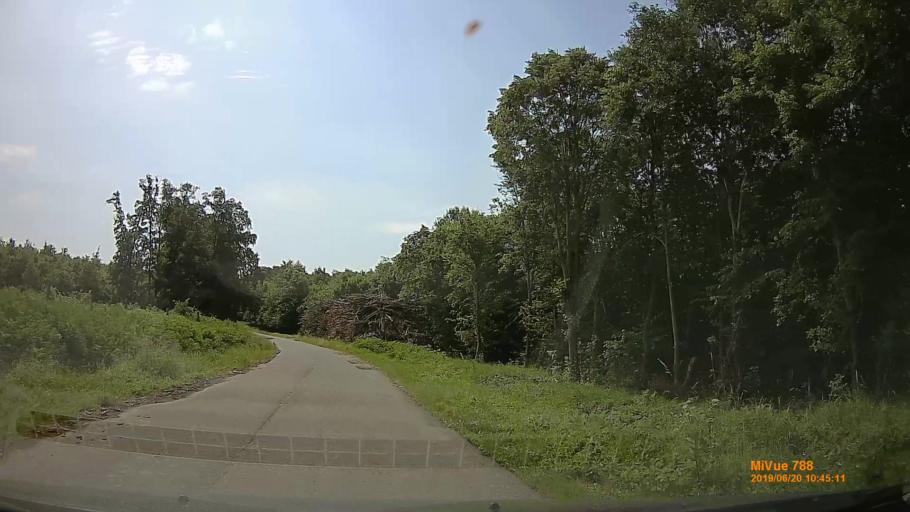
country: HU
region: Baranya
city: Hidas
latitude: 46.1843
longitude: 18.5695
